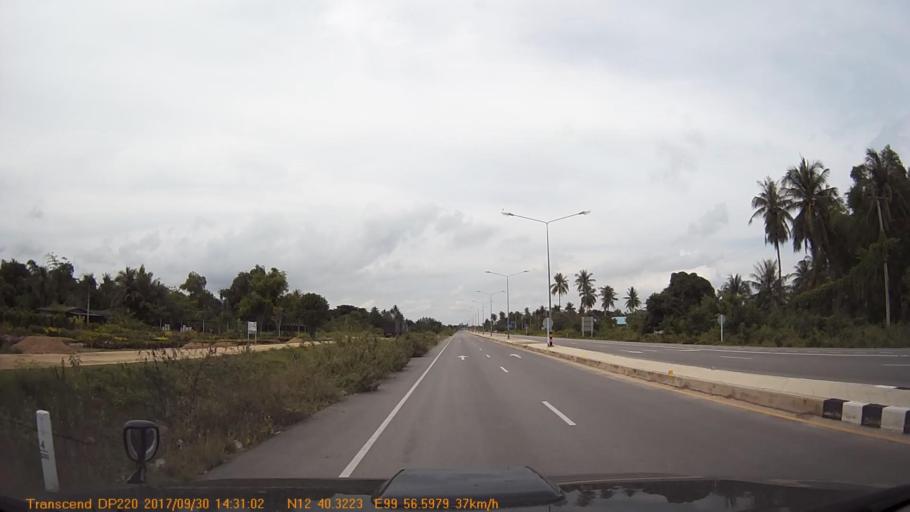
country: TH
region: Prachuap Khiri Khan
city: Hua Hin
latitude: 12.6725
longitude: 99.9432
